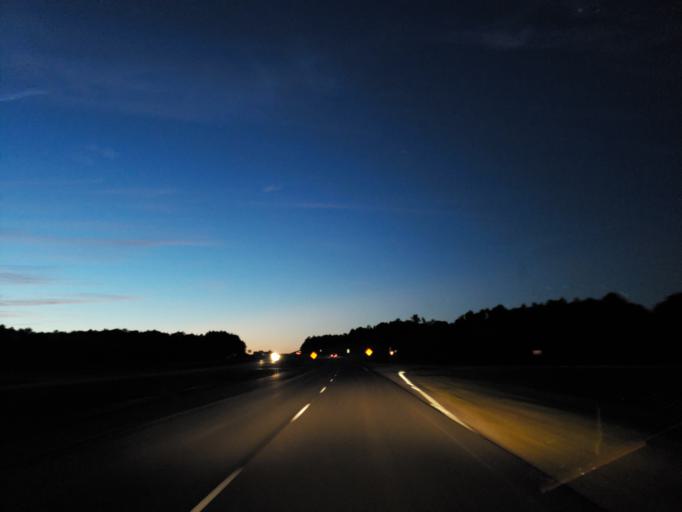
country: US
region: Mississippi
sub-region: Clarke County
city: Quitman
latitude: 32.1007
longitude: -88.7062
